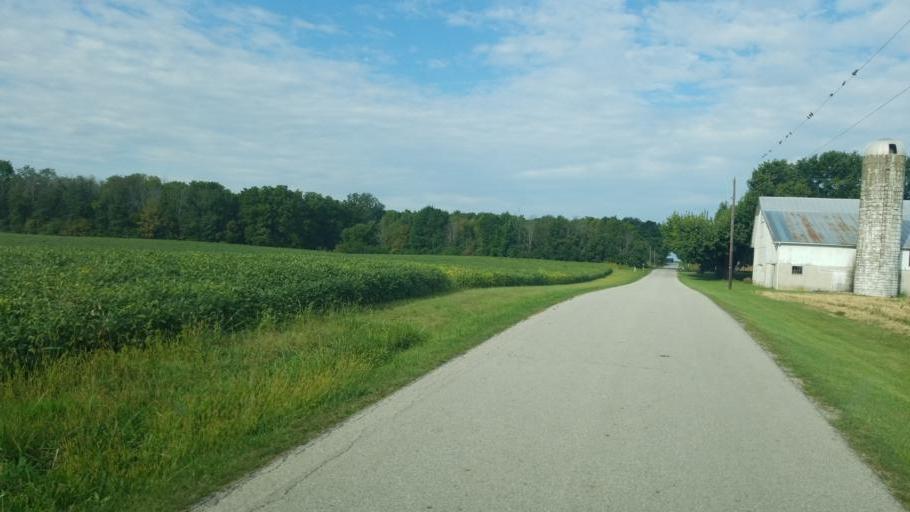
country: US
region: Ohio
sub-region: Crawford County
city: Bucyrus
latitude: 40.7322
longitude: -83.0398
